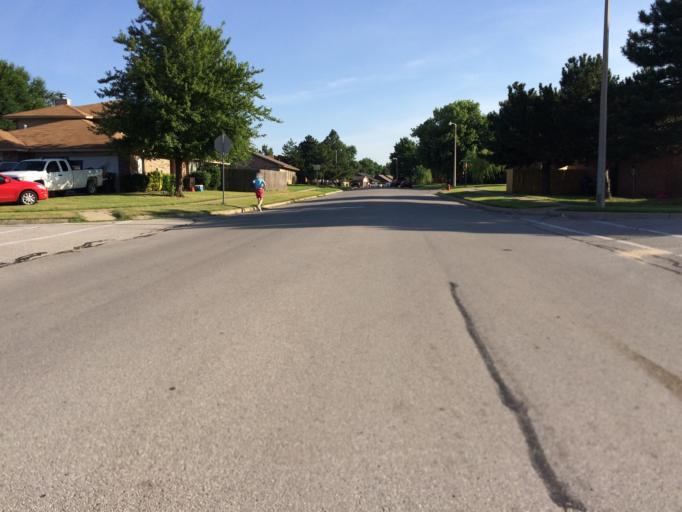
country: US
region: Oklahoma
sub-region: Cleveland County
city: Norman
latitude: 35.2202
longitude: -97.5045
